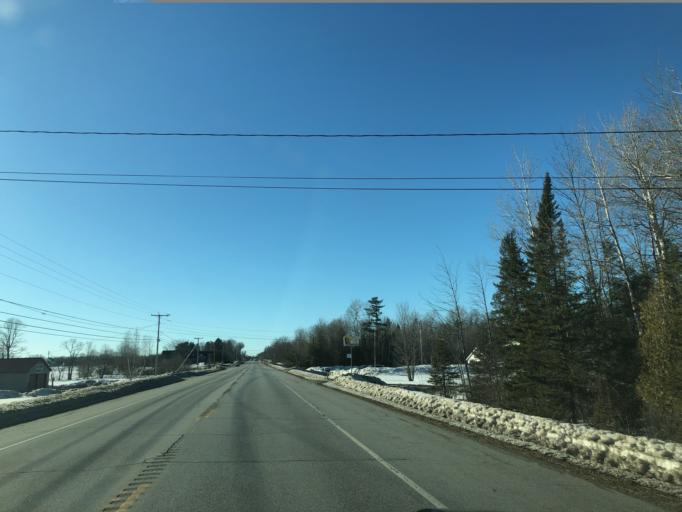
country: US
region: Maine
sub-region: Penobscot County
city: Kenduskeag
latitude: 44.9794
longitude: -68.9940
